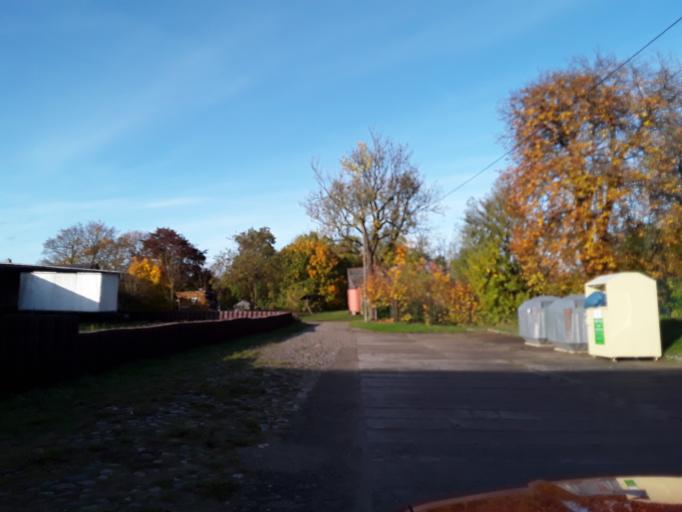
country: DE
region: Brandenburg
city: Gerswalde
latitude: 53.2866
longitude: 13.7302
